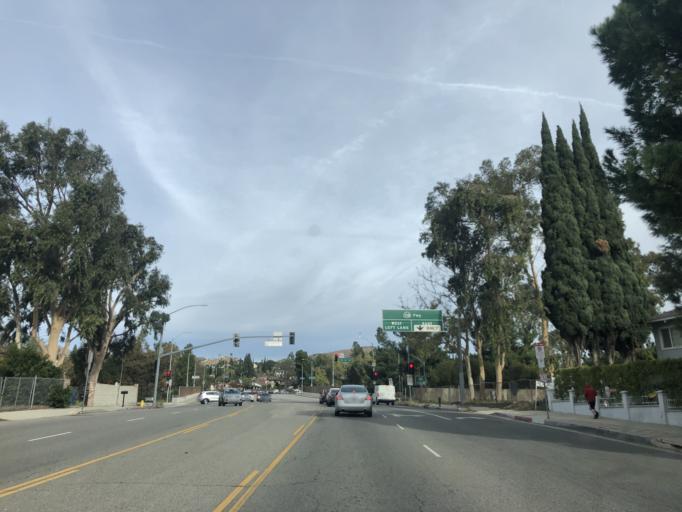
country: US
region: California
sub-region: Los Angeles County
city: Northridge
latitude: 34.2739
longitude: -118.5361
